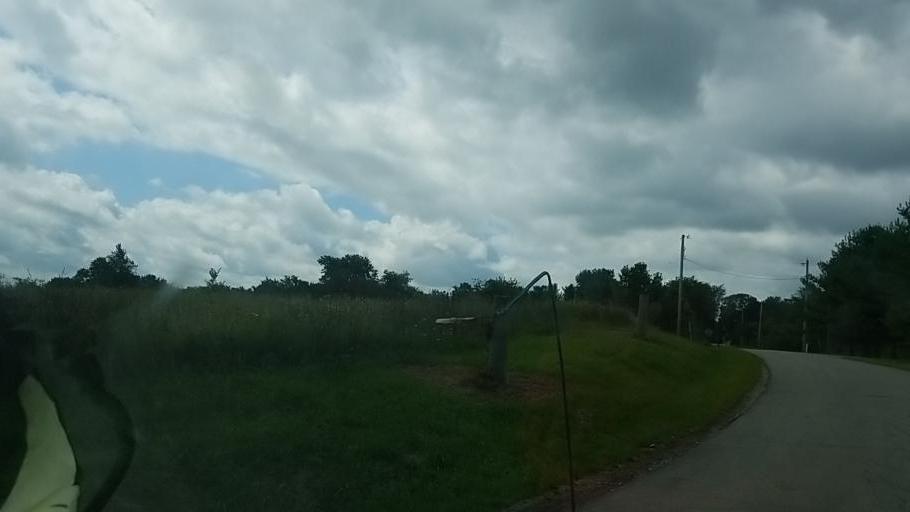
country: US
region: Ohio
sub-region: Madison County
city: Bethel
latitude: 39.6889
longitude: -83.4684
